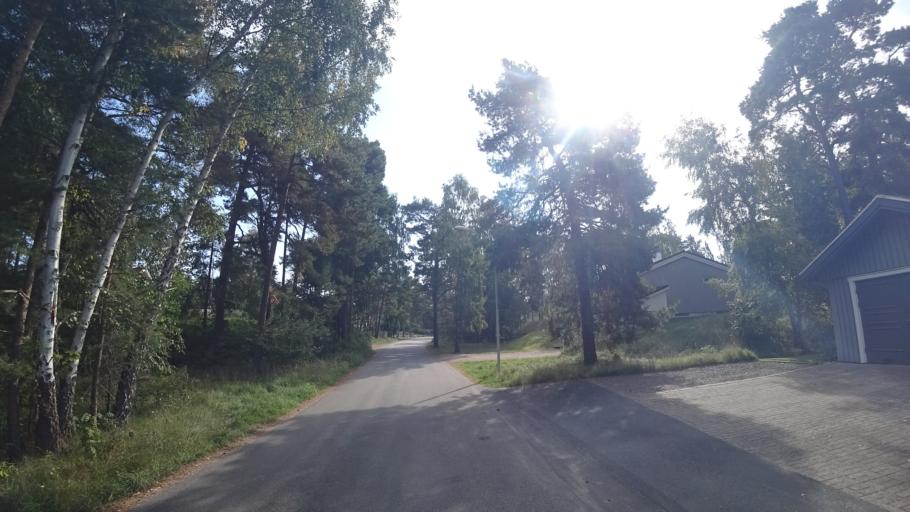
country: SE
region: Skane
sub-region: Kristianstads Kommun
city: Ahus
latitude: 55.9179
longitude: 14.2969
